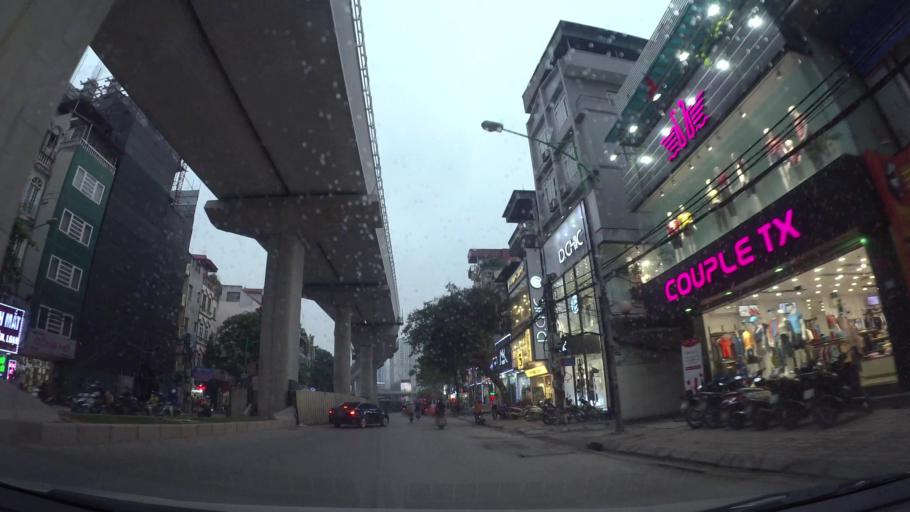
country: VN
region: Ha Noi
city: Cau Giay
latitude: 21.0313
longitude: 105.8001
